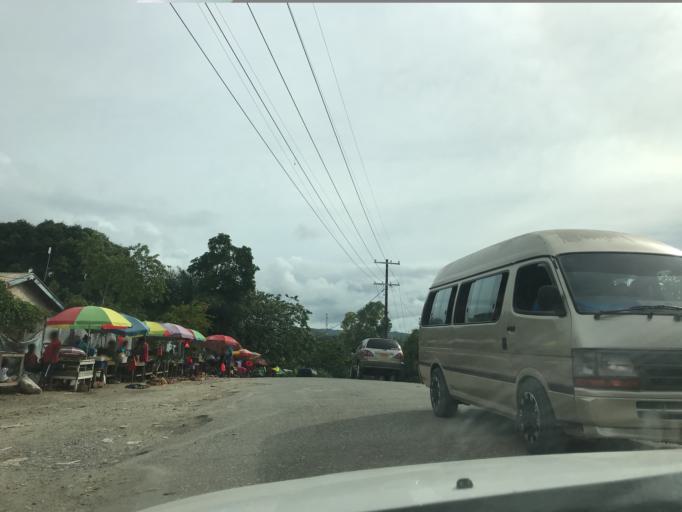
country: SB
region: Guadalcanal
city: Honiara
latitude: -9.4369
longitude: 159.9439
